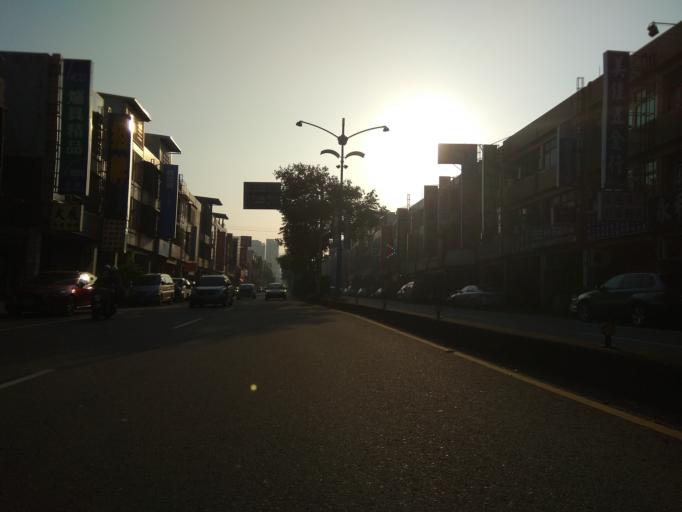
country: TW
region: Taiwan
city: Daxi
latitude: 24.9213
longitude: 121.1860
